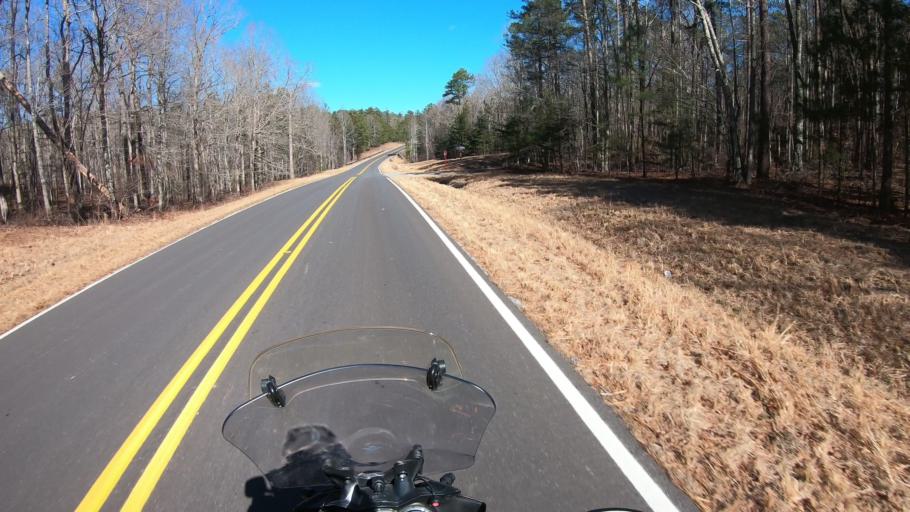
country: US
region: Alabama
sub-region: Talladega County
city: Munford
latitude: 33.4417
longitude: -85.8435
